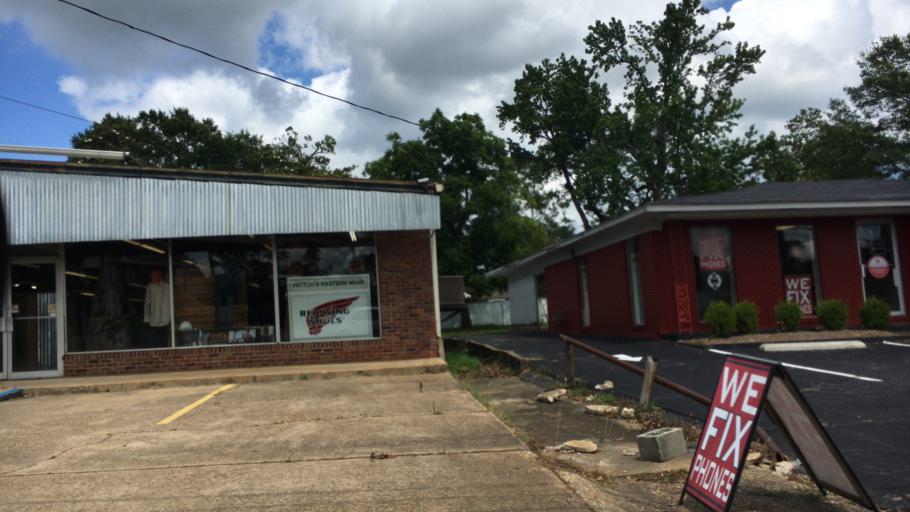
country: US
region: Louisiana
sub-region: Lincoln Parish
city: Ruston
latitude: 32.5362
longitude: -92.6387
